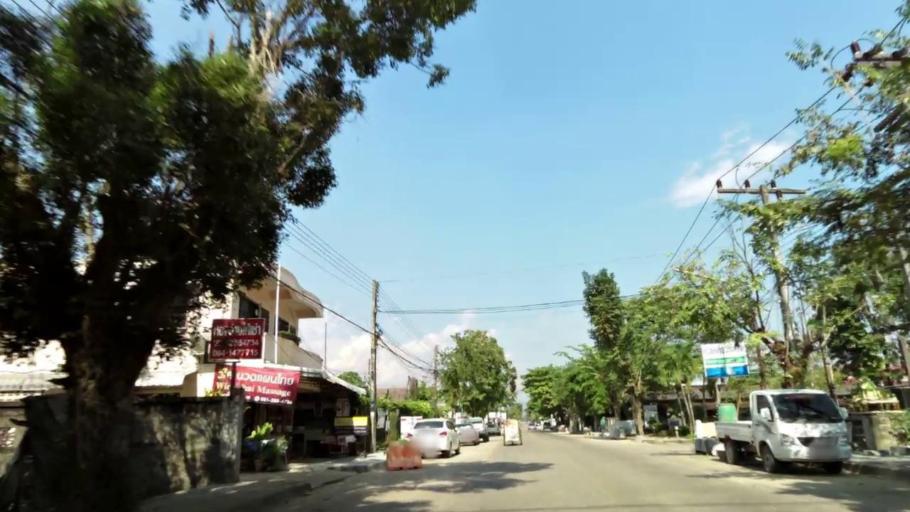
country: TH
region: Chiang Rai
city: Chiang Rai
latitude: 19.8942
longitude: 99.8274
